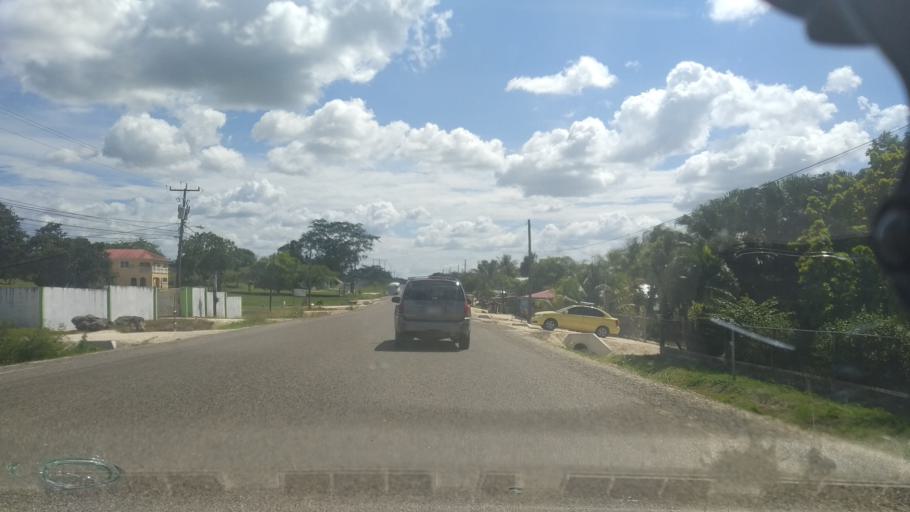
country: BZ
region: Cayo
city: Belmopan
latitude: 17.2567
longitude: -88.8074
